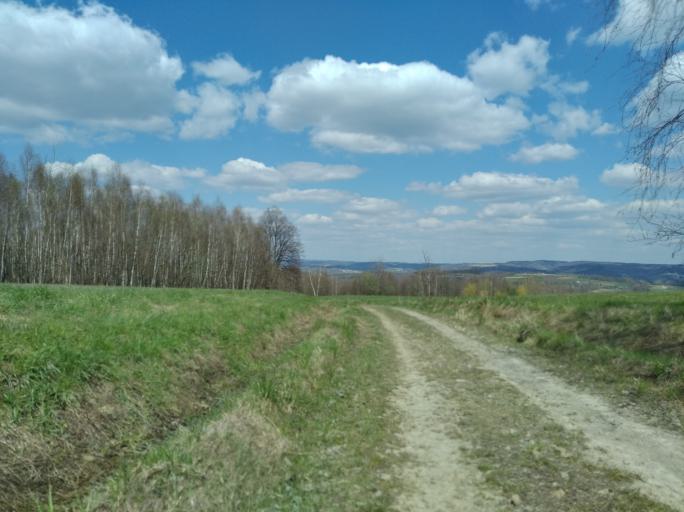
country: PL
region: Subcarpathian Voivodeship
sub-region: Powiat strzyzowski
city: Wysoka Strzyzowska
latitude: 49.8349
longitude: 21.7676
